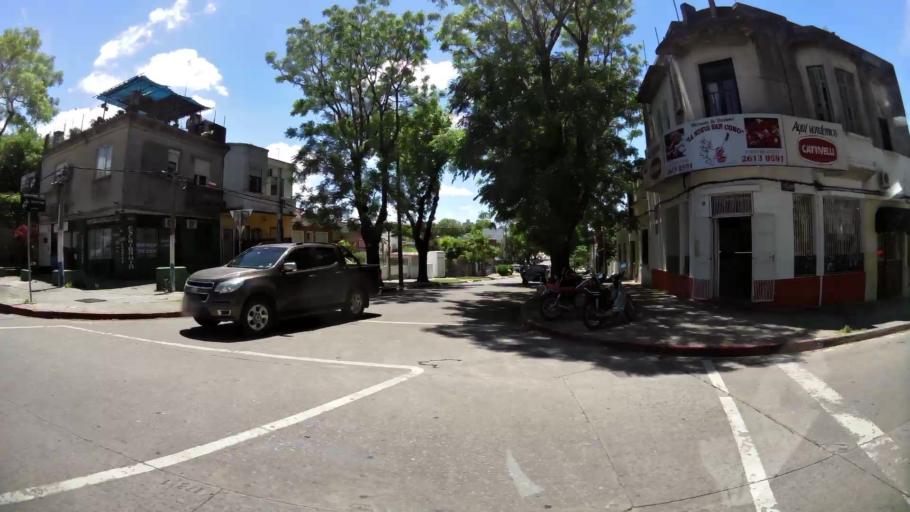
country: UY
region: Montevideo
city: Montevideo
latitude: -34.8931
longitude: -56.1242
